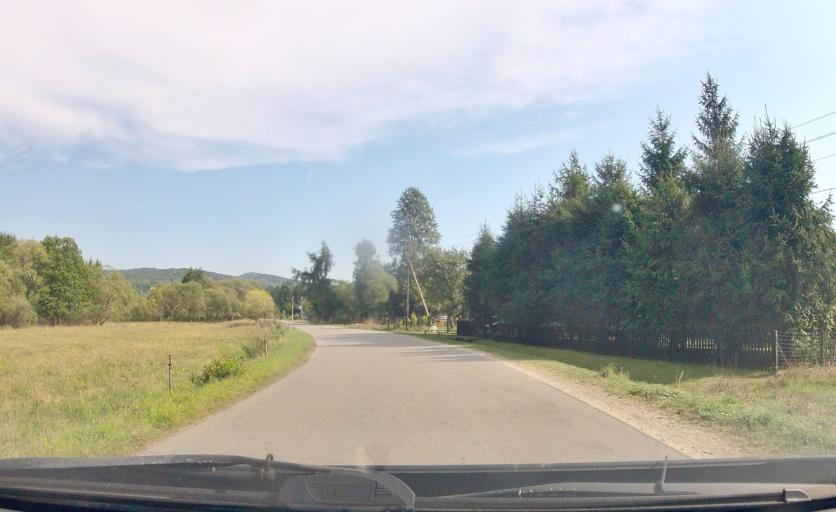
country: PL
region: Subcarpathian Voivodeship
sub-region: Powiat jasielski
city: Krempna
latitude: 49.4972
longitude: 21.5546
